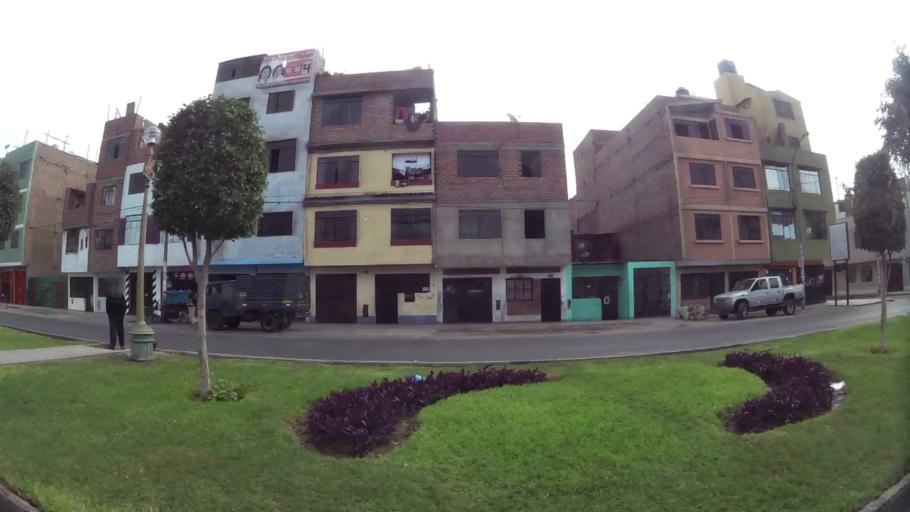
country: PE
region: Callao
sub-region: Callao
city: Callao
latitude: -12.0270
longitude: -77.0953
